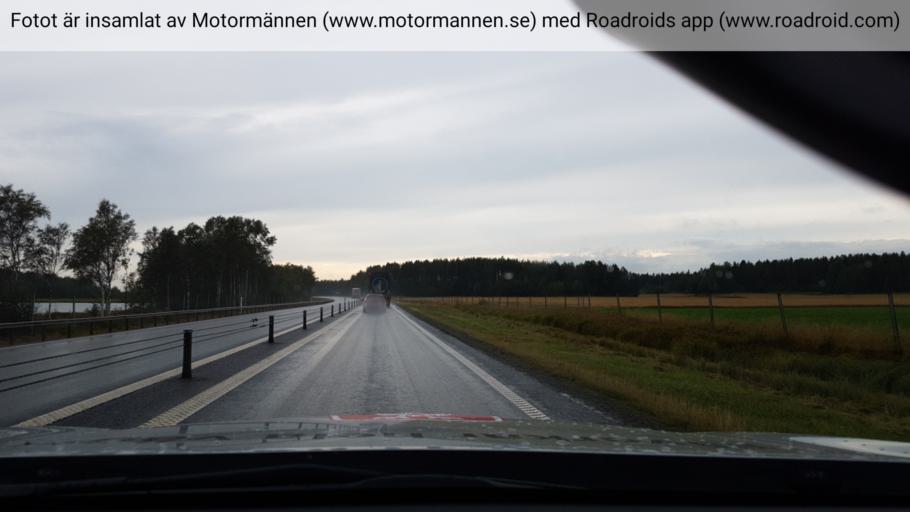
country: SE
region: Vaesterbotten
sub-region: Robertsfors Kommun
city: Robertsfors
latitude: 64.1473
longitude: 20.8996
